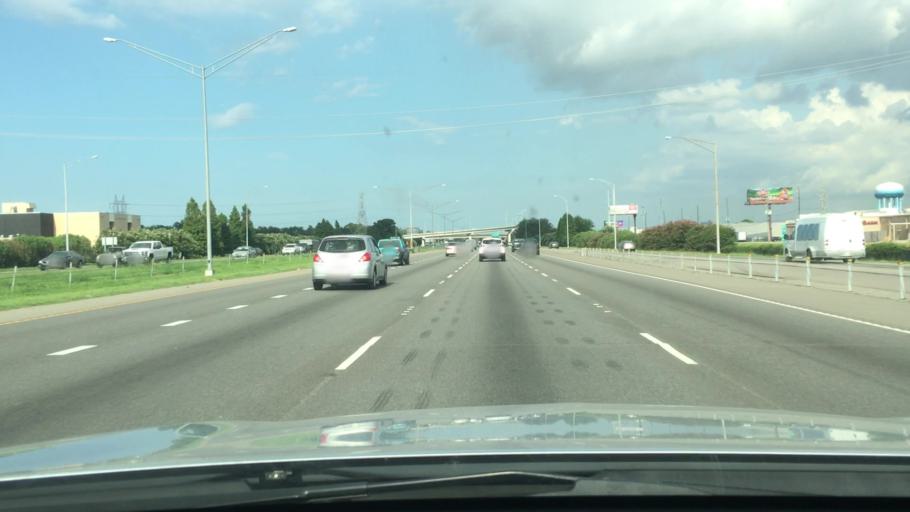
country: US
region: Louisiana
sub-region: Jefferson Parish
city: Kenner
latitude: 30.0085
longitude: -90.2294
